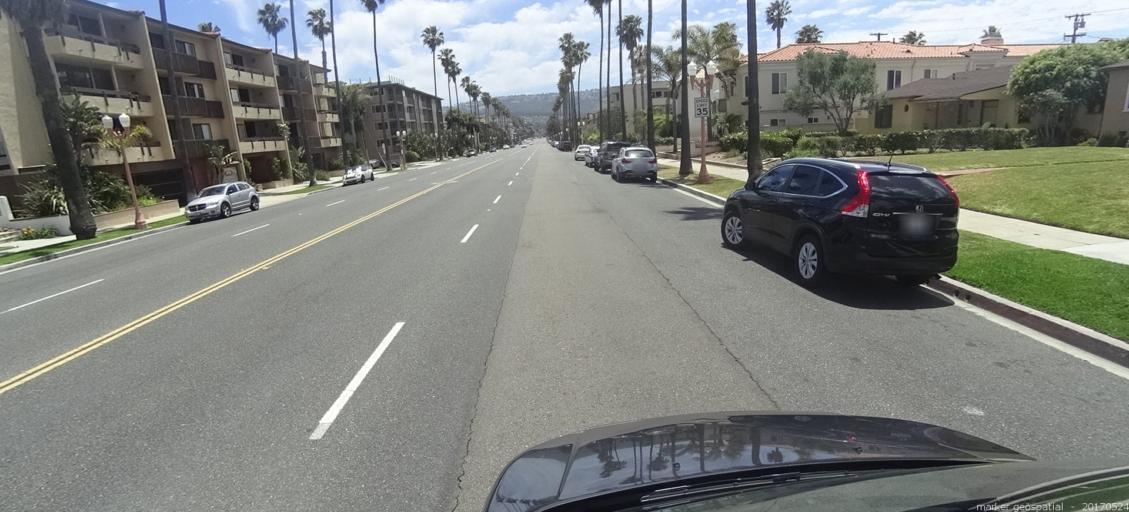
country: US
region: California
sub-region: Los Angeles County
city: Redondo Beach
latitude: 33.8253
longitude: -118.3887
